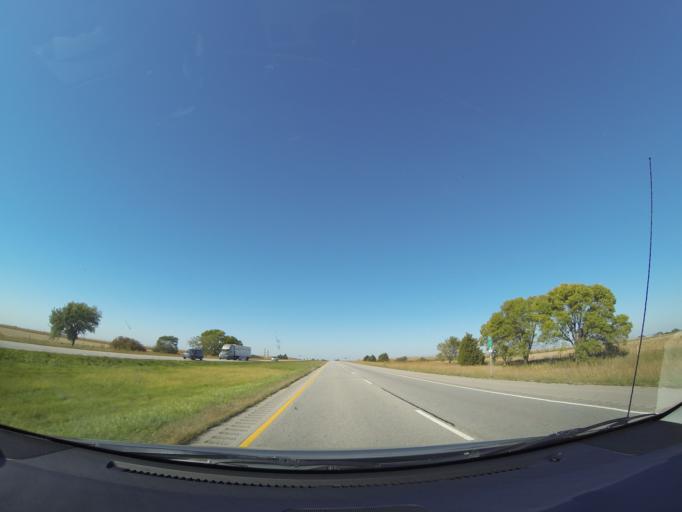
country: US
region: Nebraska
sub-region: Seward County
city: Milford
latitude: 40.8224
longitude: -97.1228
